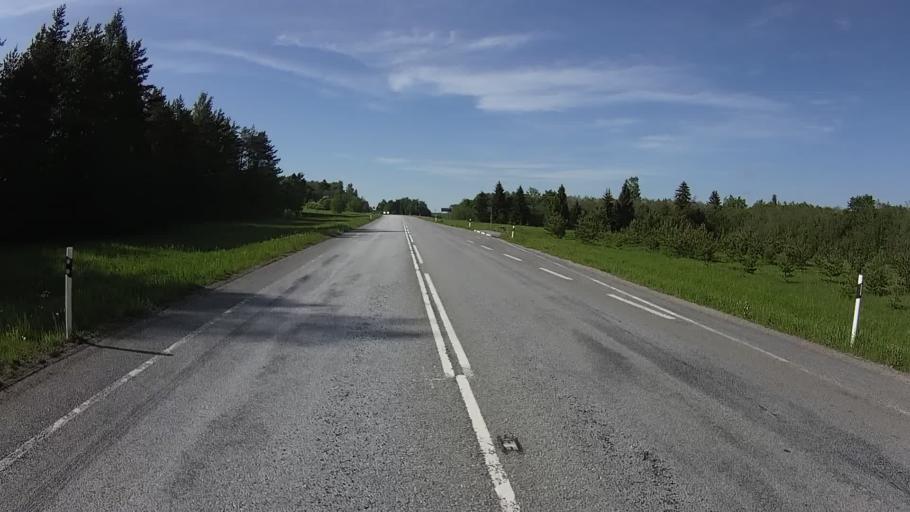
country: EE
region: Laeaene-Virumaa
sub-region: Haljala vald
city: Haljala
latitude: 59.3955
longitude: 26.3093
